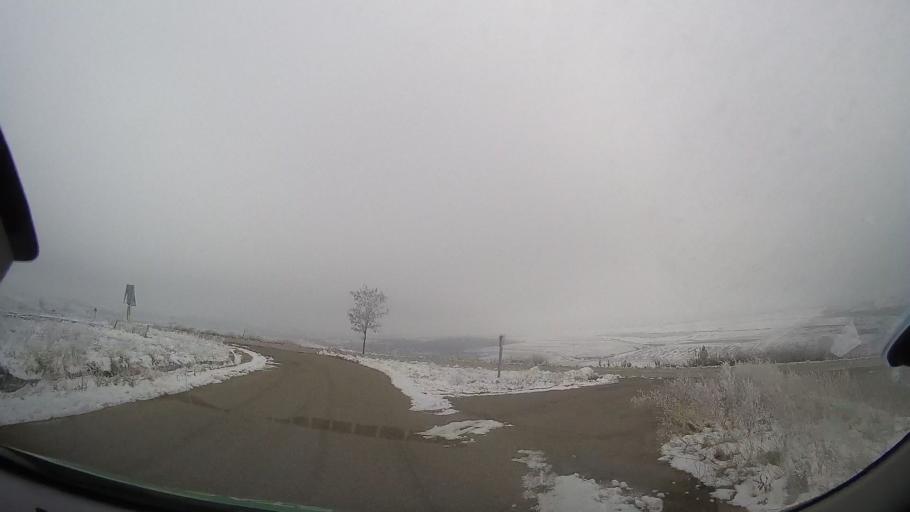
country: RO
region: Vaslui
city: Coroiesti
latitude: 46.2120
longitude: 27.4816
